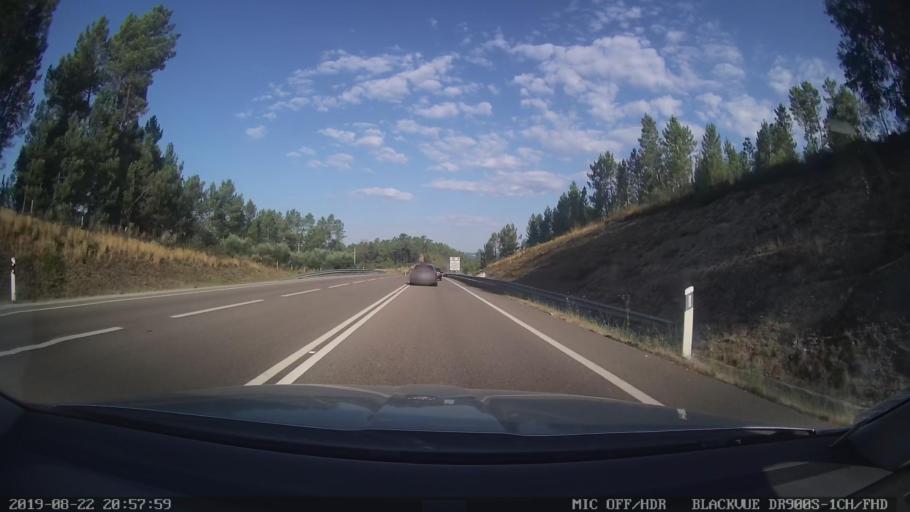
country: PT
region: Castelo Branco
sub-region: Serta
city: Serta
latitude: 39.7971
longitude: -8.0747
